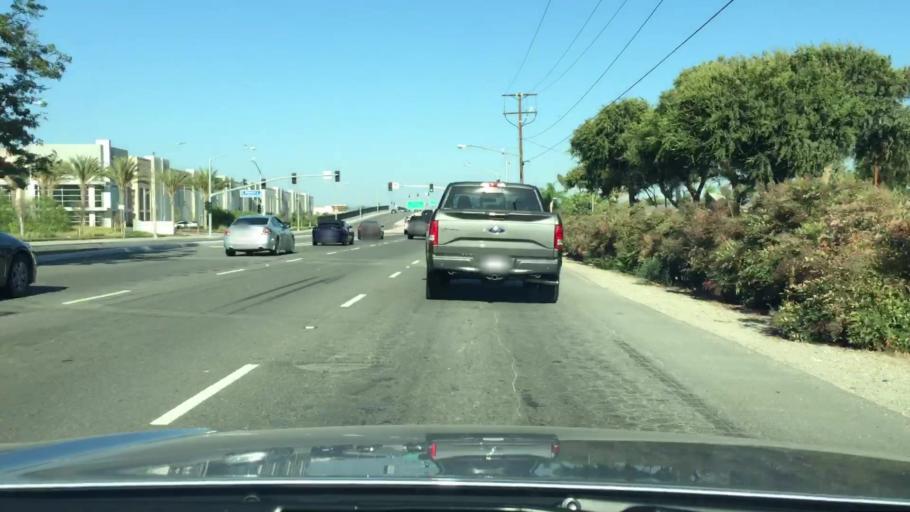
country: US
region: California
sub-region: Los Angeles County
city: Diamond Bar
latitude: 34.0527
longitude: -117.7867
